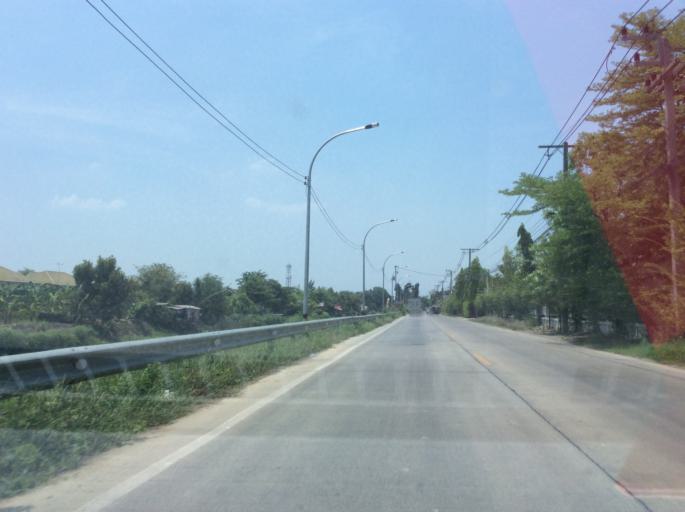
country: TH
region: Pathum Thani
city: Ban Rangsit
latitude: 14.0319
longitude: 100.7786
